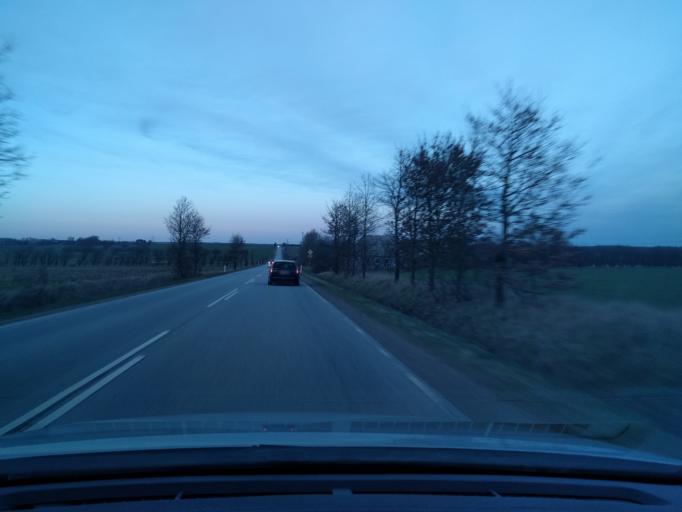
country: DK
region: South Denmark
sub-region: Vejen Kommune
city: Rodding
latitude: 55.3274
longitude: 9.1498
